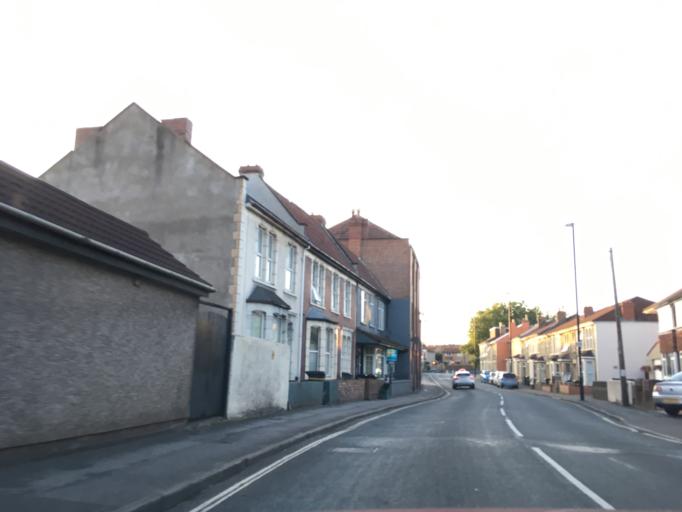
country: GB
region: England
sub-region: Bristol
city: Bristol
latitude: 51.4606
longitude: -2.5527
